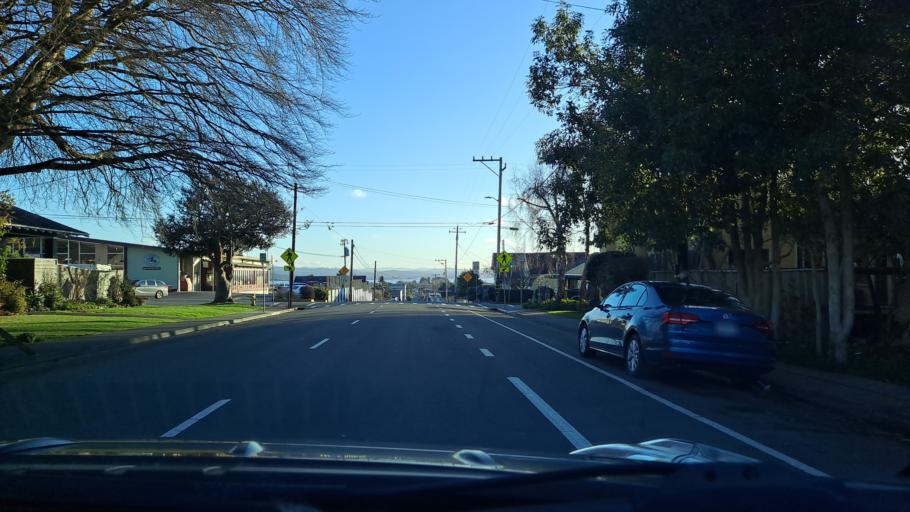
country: US
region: California
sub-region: Humboldt County
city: Arcata
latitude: 40.8726
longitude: -124.0855
